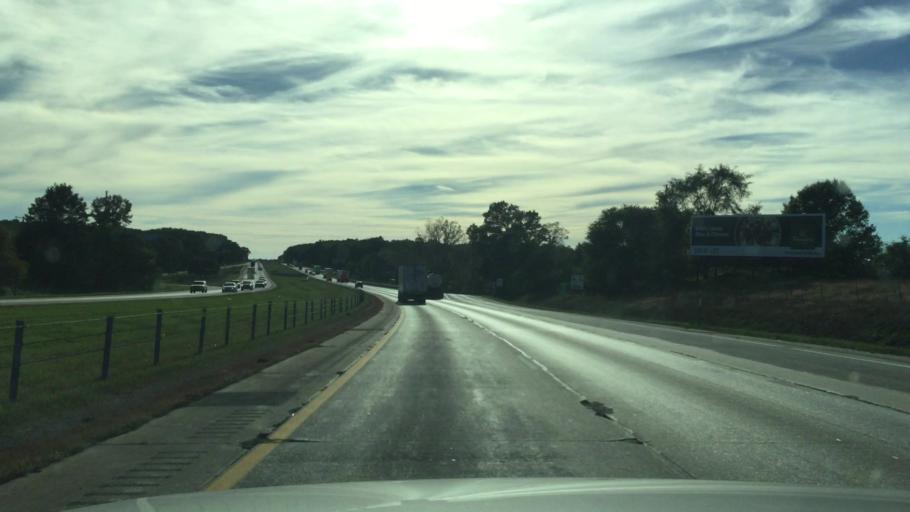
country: US
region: Michigan
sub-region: Calhoun County
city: Brownlee Park
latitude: 42.2840
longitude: -85.1516
